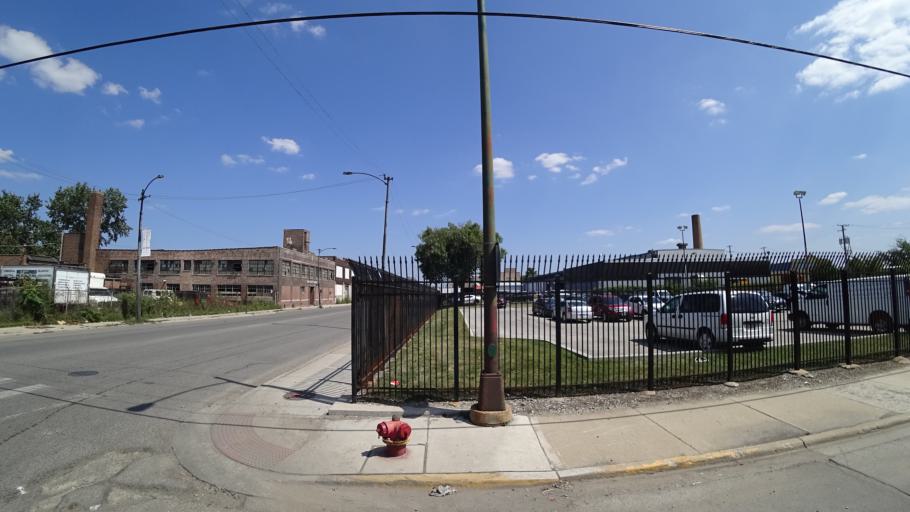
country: US
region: Illinois
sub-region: Cook County
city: Cicero
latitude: 41.8659
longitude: -87.7374
